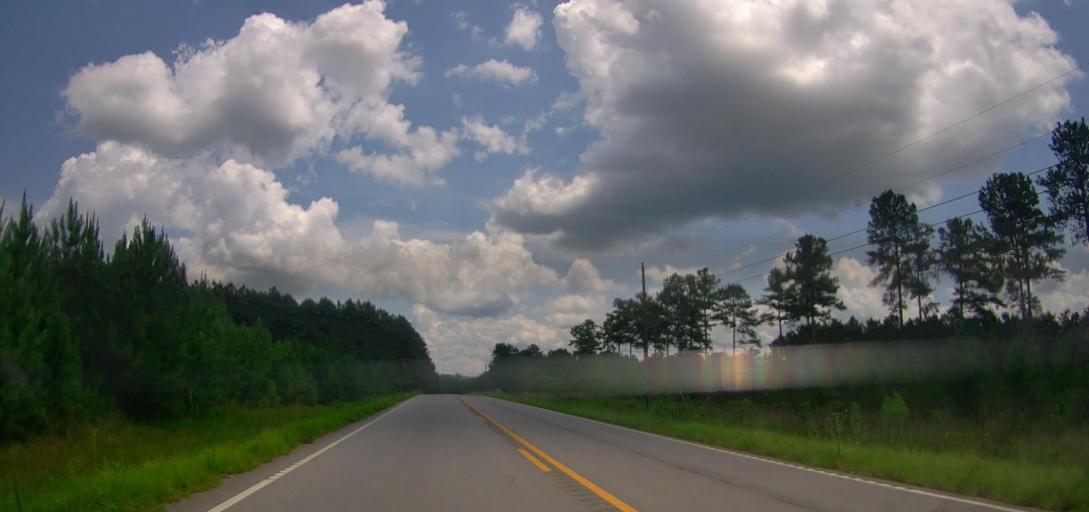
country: US
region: Georgia
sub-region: Meriwether County
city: Greenville
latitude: 33.0209
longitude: -84.6811
